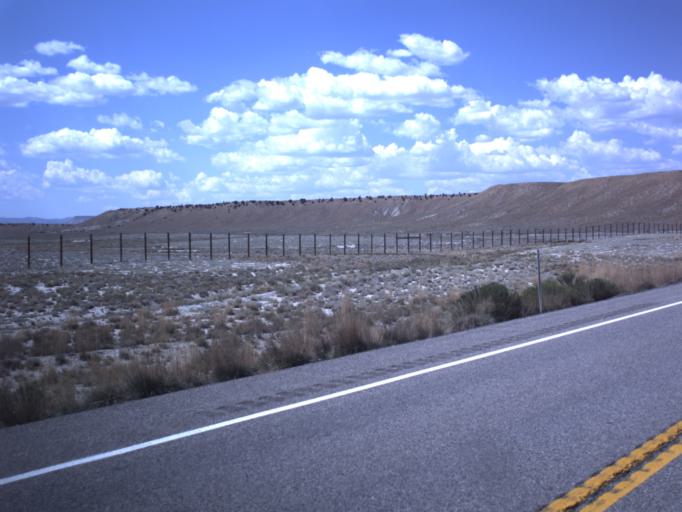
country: US
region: Utah
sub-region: Carbon County
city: Price
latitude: 39.4616
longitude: -110.8595
